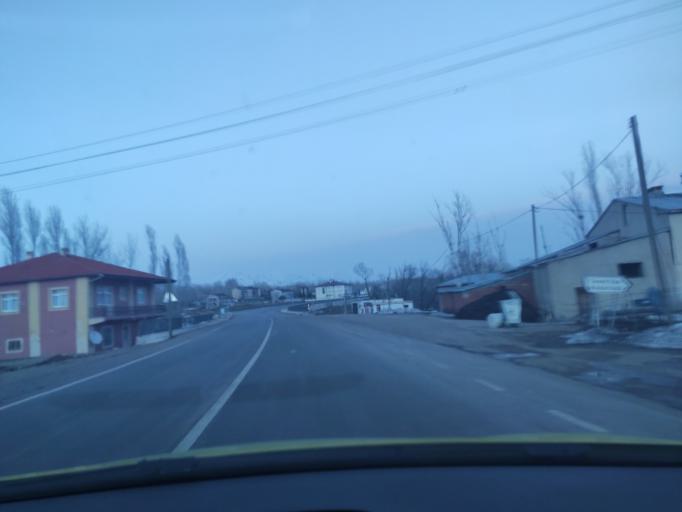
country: TR
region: Bayburt
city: Aydintepe
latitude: 40.3859
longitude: 40.1354
